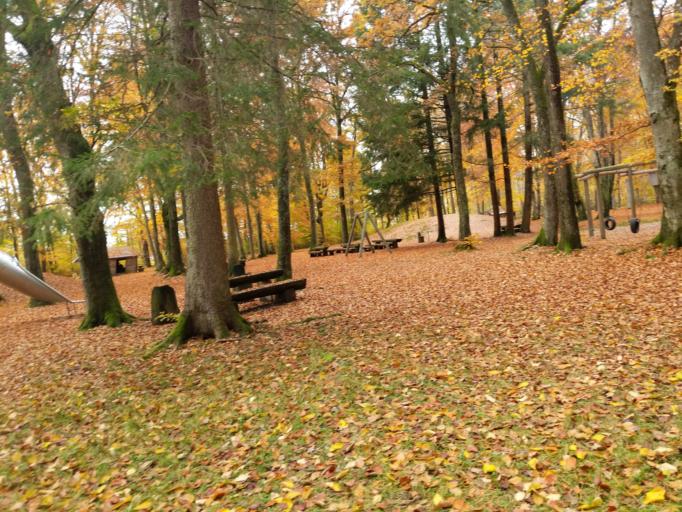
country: DE
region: Bavaria
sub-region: Upper Bavaria
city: Zorneding
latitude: 48.0962
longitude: 11.8429
